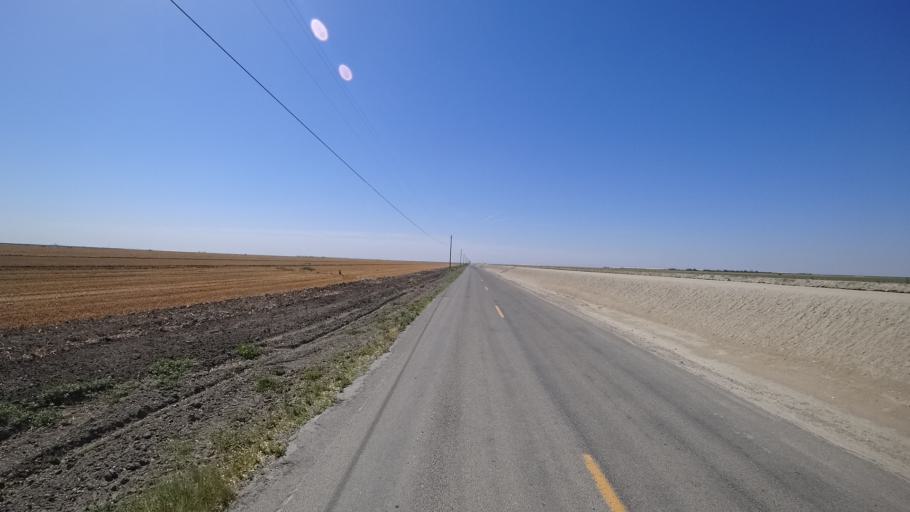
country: US
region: California
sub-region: Kings County
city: Corcoran
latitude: 36.0197
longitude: -119.5361
